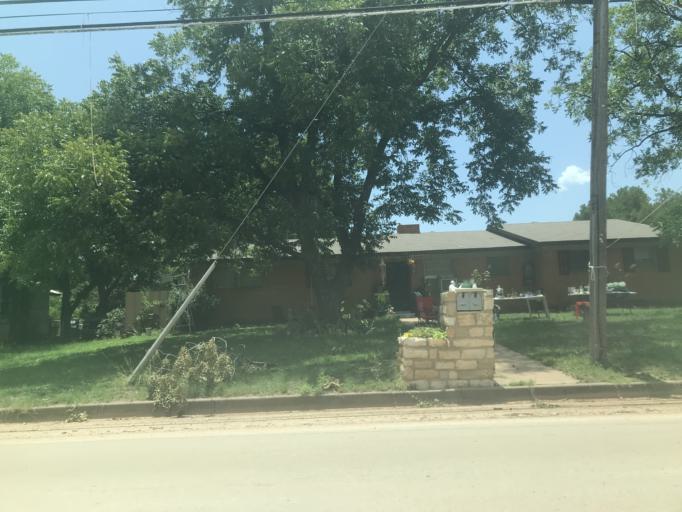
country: US
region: Texas
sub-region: Taylor County
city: Abilene
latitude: 32.4638
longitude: -99.7199
